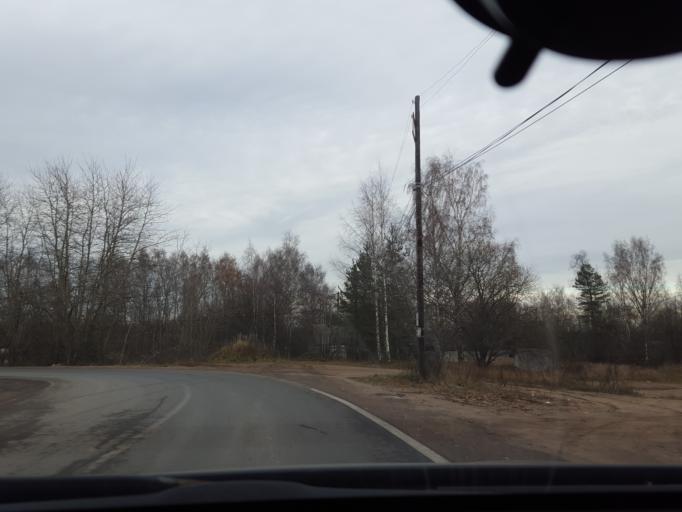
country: RU
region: St.-Petersburg
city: Shuvalovo
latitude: 60.0449
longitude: 30.2670
